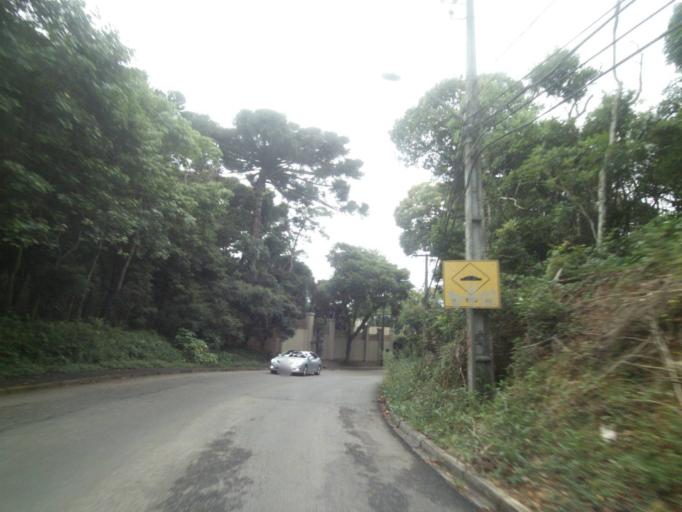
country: BR
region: Parana
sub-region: Curitiba
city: Curitiba
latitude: -25.4538
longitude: -49.3336
